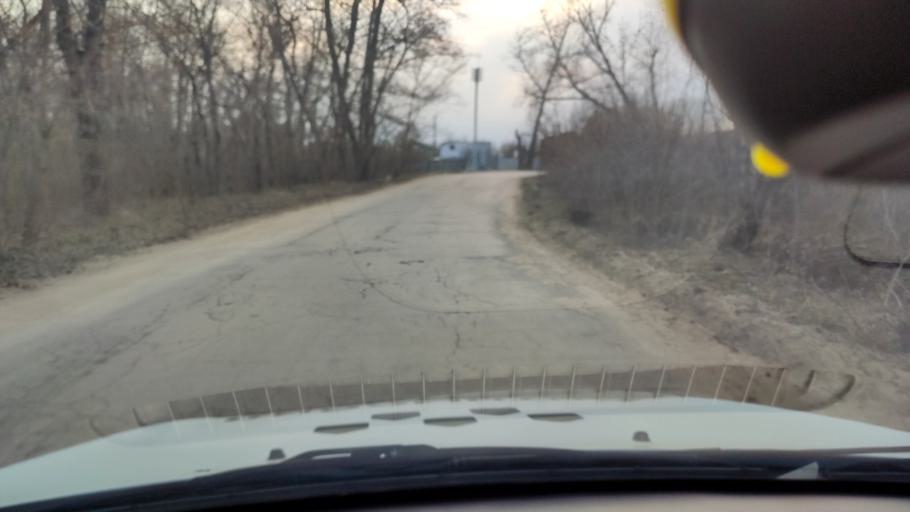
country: RU
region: Samara
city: Zhigulevsk
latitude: 53.4527
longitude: 49.5635
